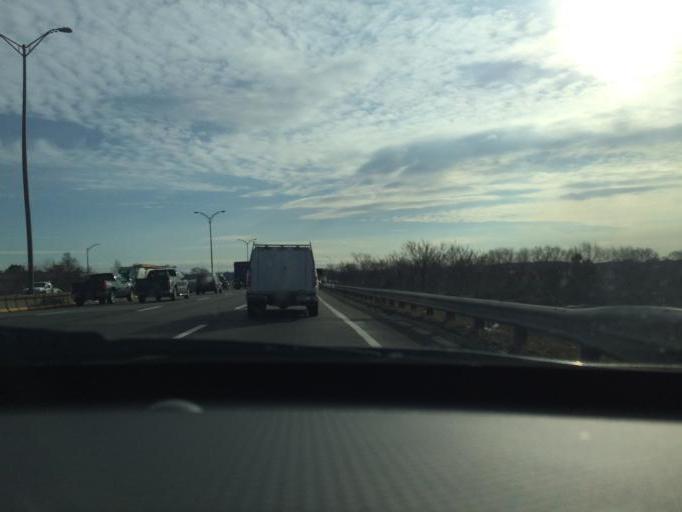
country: US
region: Massachusetts
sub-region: Suffolk County
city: South Boston
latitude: 42.2900
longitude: -71.0438
